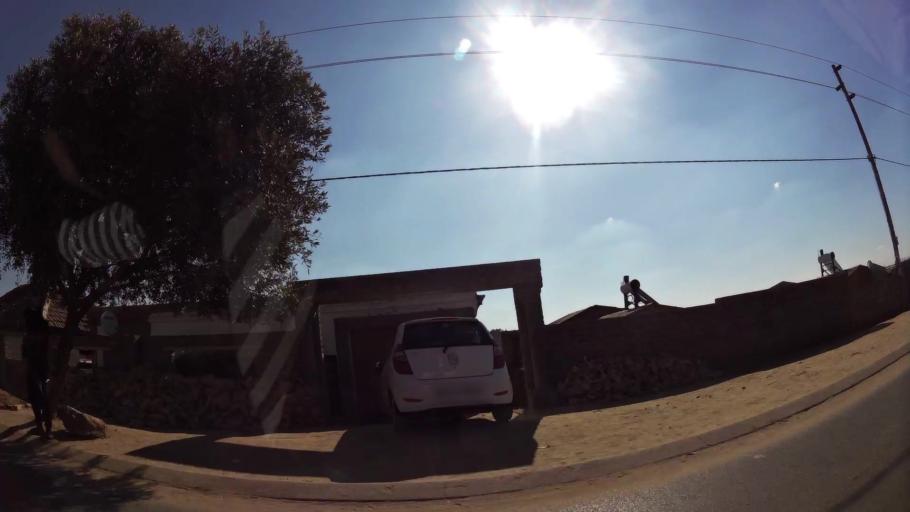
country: ZA
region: Gauteng
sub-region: West Rand District Municipality
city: Muldersdriseloop
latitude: -26.0193
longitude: 27.9219
